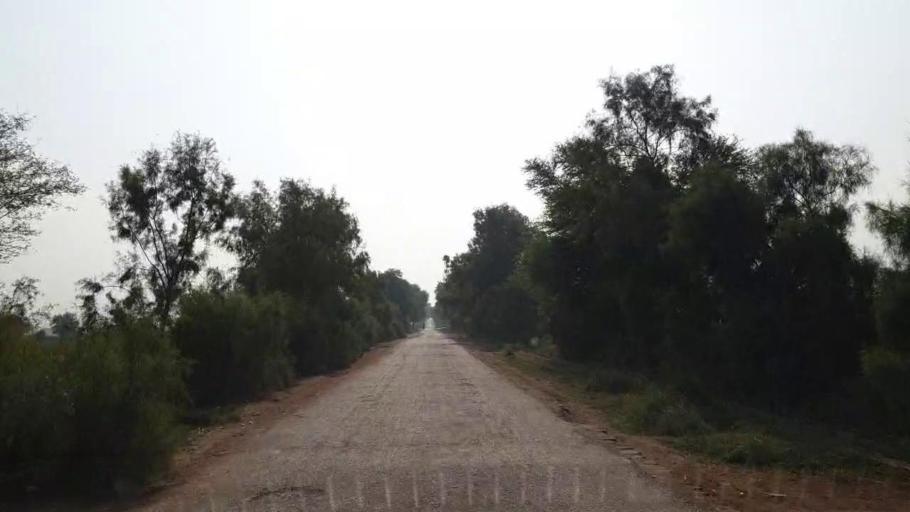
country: PK
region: Sindh
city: Bhan
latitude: 26.4747
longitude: 67.7734
